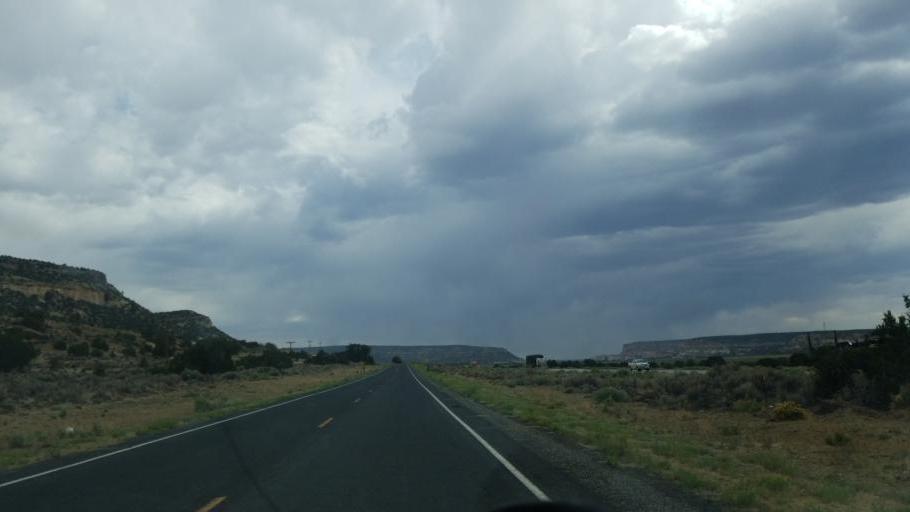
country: US
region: Arizona
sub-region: Apache County
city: Houck
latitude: 35.4051
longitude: -109.0004
